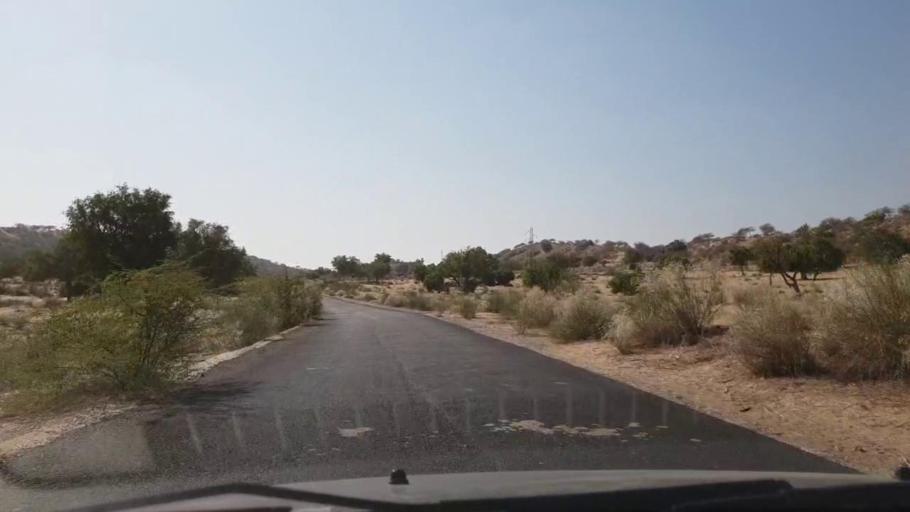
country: PK
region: Sindh
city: Mithi
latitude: 24.6805
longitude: 69.7781
